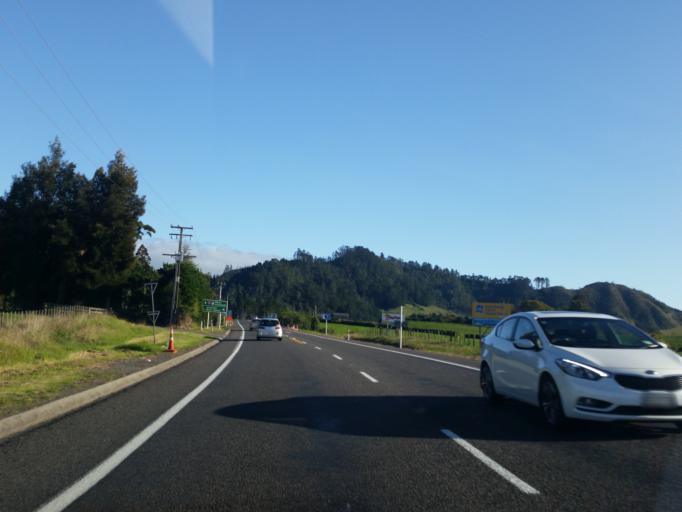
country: NZ
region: Bay of Plenty
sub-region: Western Bay of Plenty District
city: Waihi Beach
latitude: -37.4620
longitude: 175.9355
